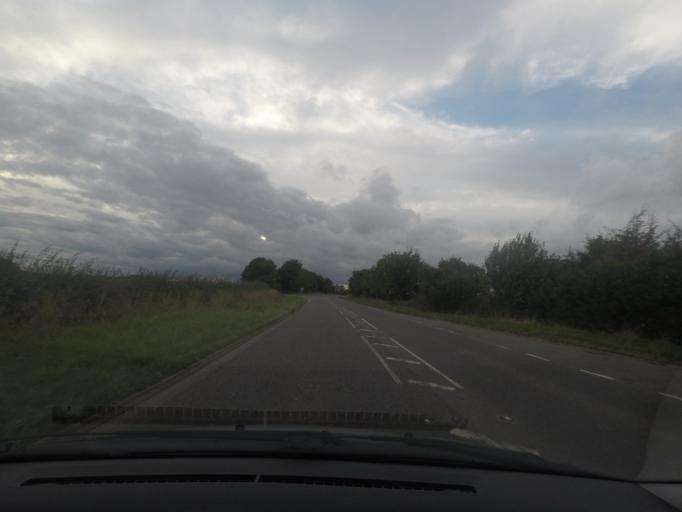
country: GB
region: England
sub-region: Lincolnshire
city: Burwell
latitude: 53.2695
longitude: 0.0750
